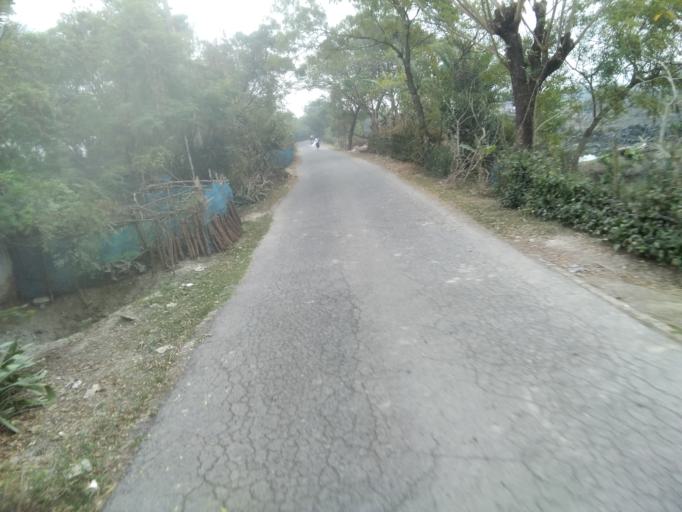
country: BD
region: Khulna
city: Satkhira
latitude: 22.5752
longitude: 89.0753
